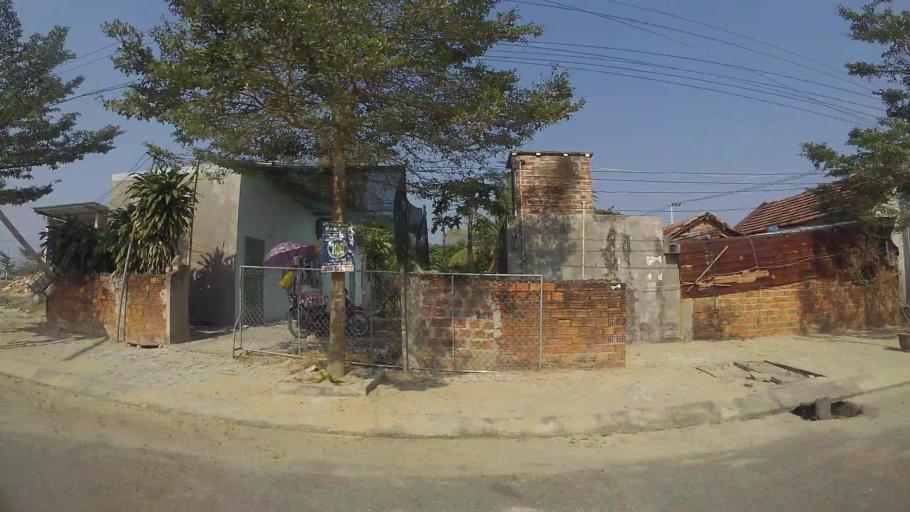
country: VN
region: Quang Nam
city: Quang Nam
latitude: 15.9523
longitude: 108.2752
